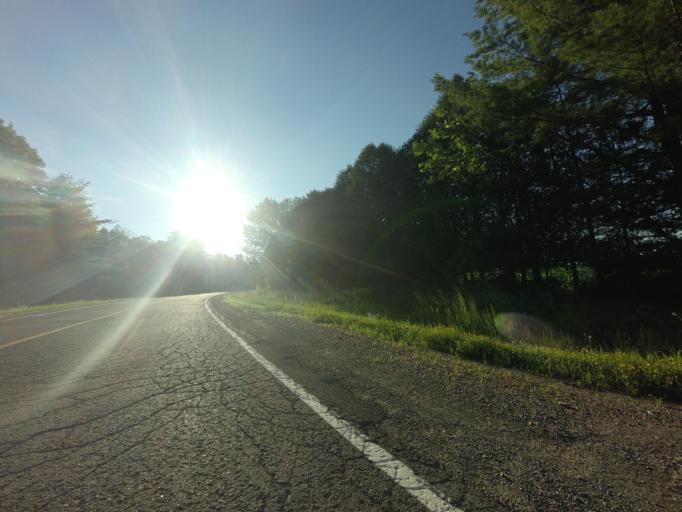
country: CA
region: Ontario
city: Arnprior
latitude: 45.3445
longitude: -76.4322
